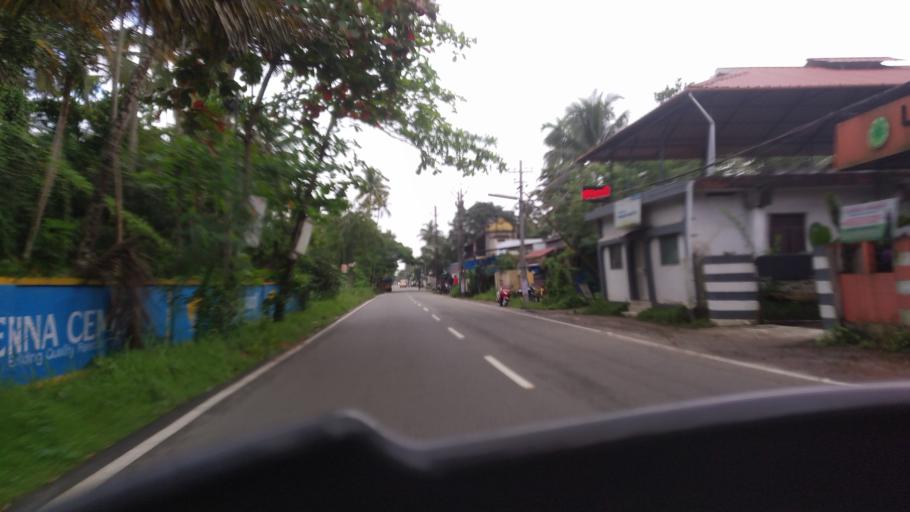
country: IN
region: Kerala
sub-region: Ernakulam
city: Elur
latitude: 10.1004
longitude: 76.2050
